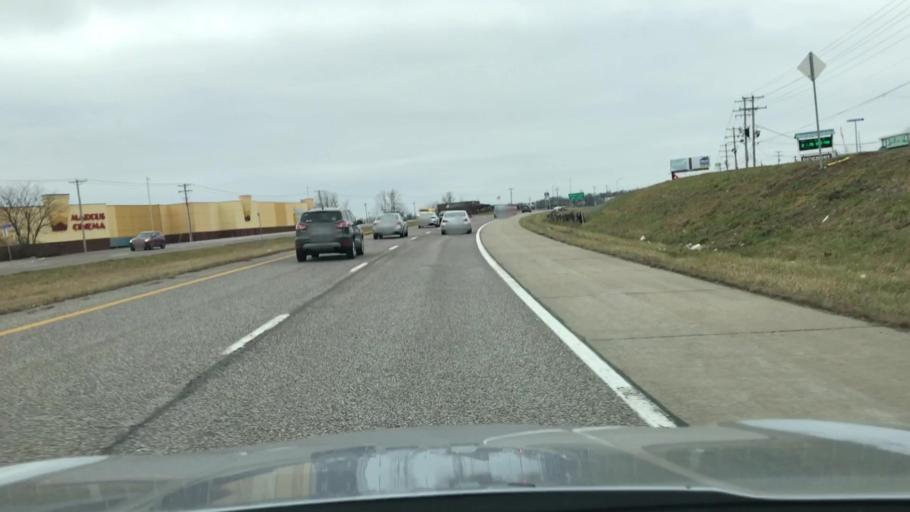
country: US
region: Missouri
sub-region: Saint Charles County
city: Saint Charles
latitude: 38.7642
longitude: -90.5267
